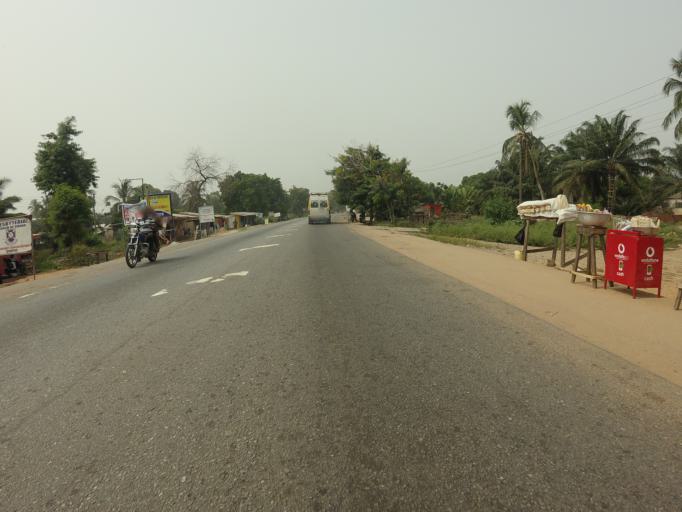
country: GH
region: Volta
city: Anloga
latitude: 5.9917
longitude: 0.5795
